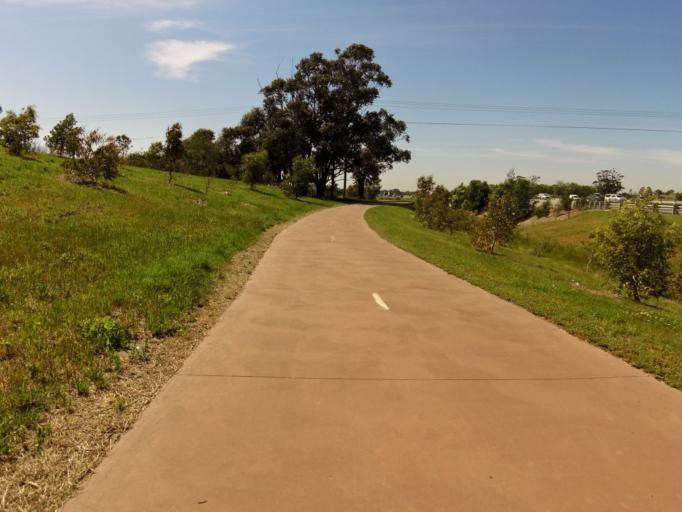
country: AU
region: Victoria
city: Heatherton
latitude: -37.9597
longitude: 145.1168
